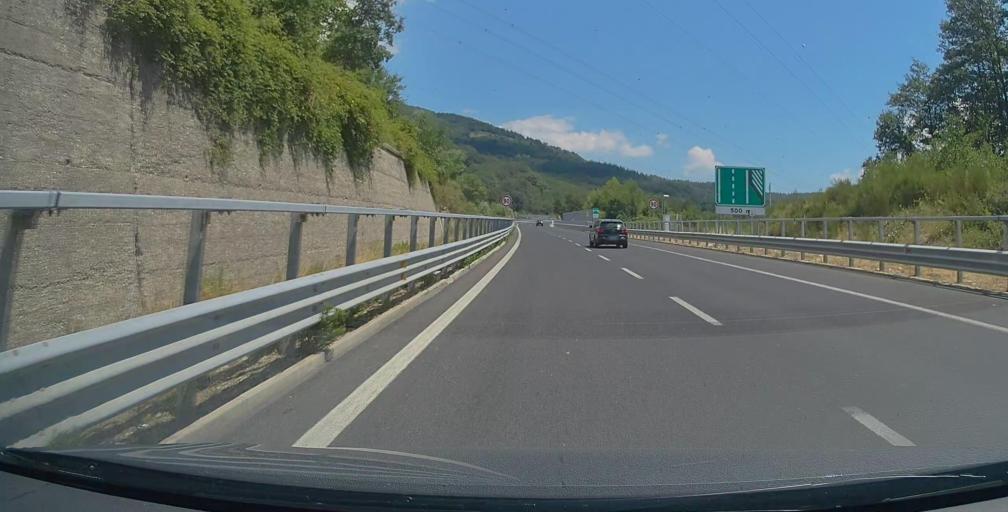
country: IT
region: Basilicate
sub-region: Provincia di Potenza
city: Nemoli
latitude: 40.0928
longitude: 15.8243
